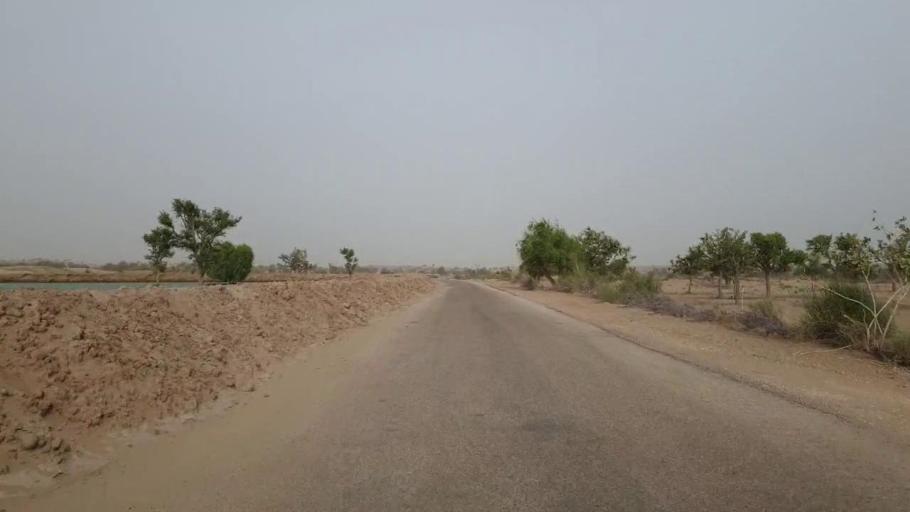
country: PK
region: Sindh
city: Islamkot
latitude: 24.5464
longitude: 70.3692
